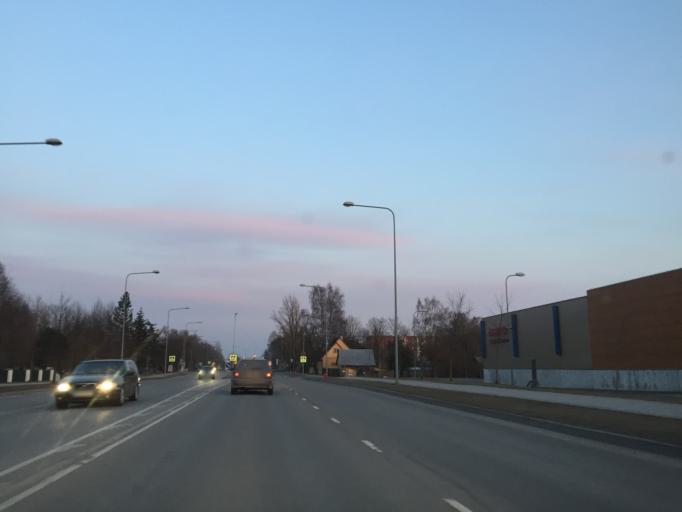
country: EE
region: Paernumaa
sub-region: Paernu linn
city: Parnu
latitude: 58.3750
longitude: 24.5377
